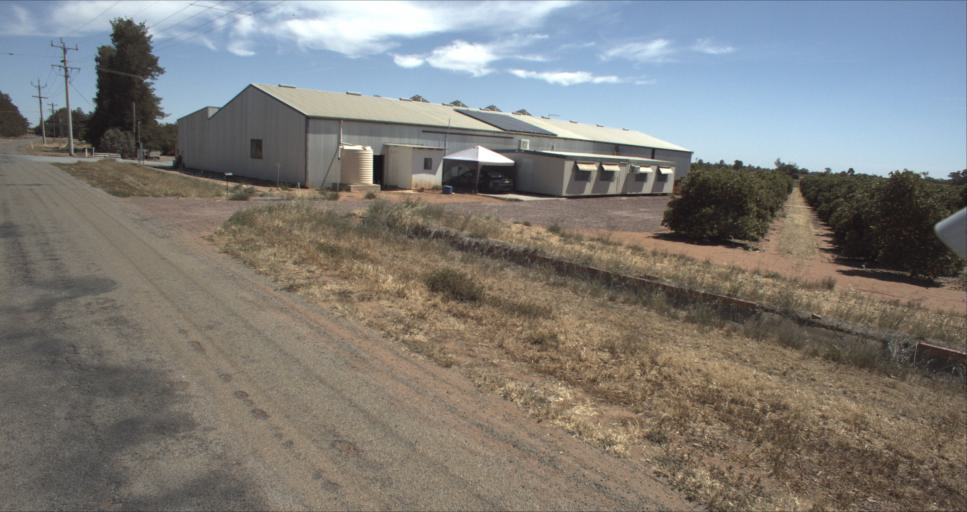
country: AU
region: New South Wales
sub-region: Leeton
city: Leeton
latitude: -34.5981
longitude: 146.4369
